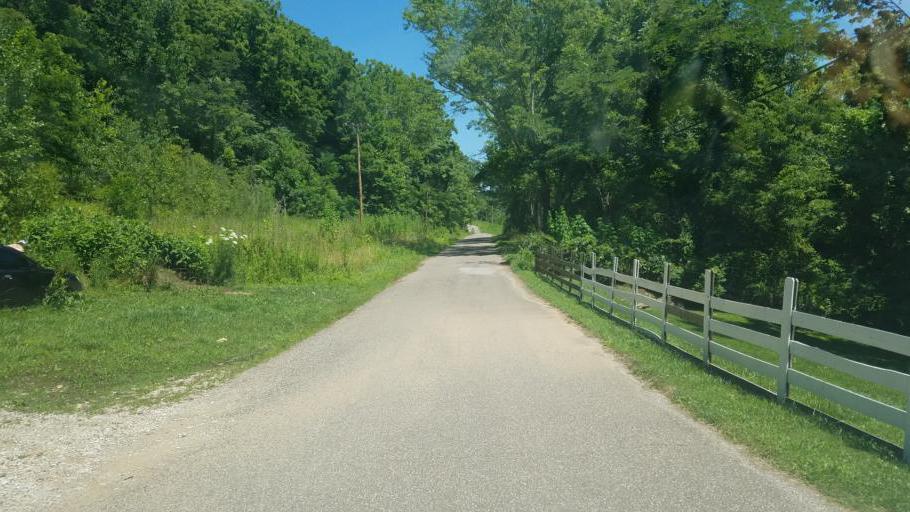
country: US
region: West Virginia
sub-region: Cabell County
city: Lesage
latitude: 38.5683
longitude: -82.2948
